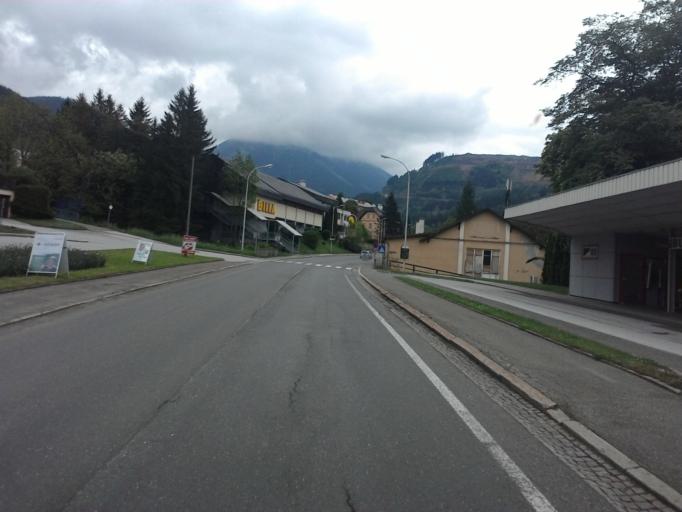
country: AT
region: Styria
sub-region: Politischer Bezirk Leoben
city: Eisenerz
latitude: 47.5426
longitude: 14.8878
